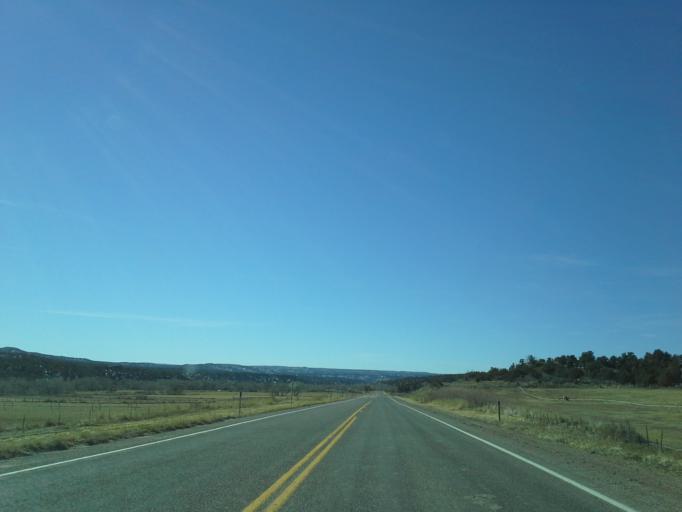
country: US
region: Utah
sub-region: Kane County
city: Kanab
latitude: 37.2704
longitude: -112.6503
